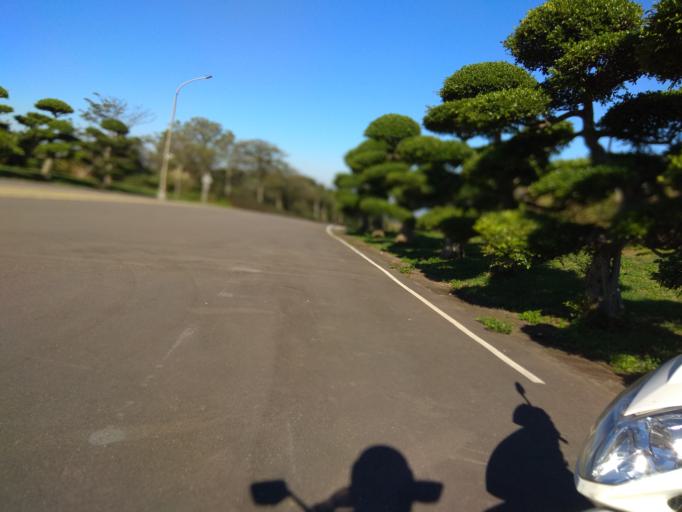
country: TW
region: Taiwan
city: Daxi
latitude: 24.8901
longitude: 121.1489
